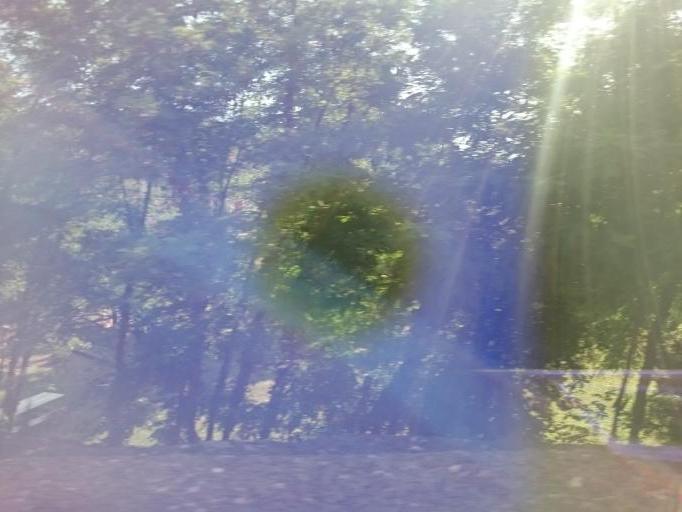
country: IT
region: Veneto
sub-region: Provincia di Verona
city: Sant'Ambrogio di Valpollicella
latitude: 45.5182
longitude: 10.8210
